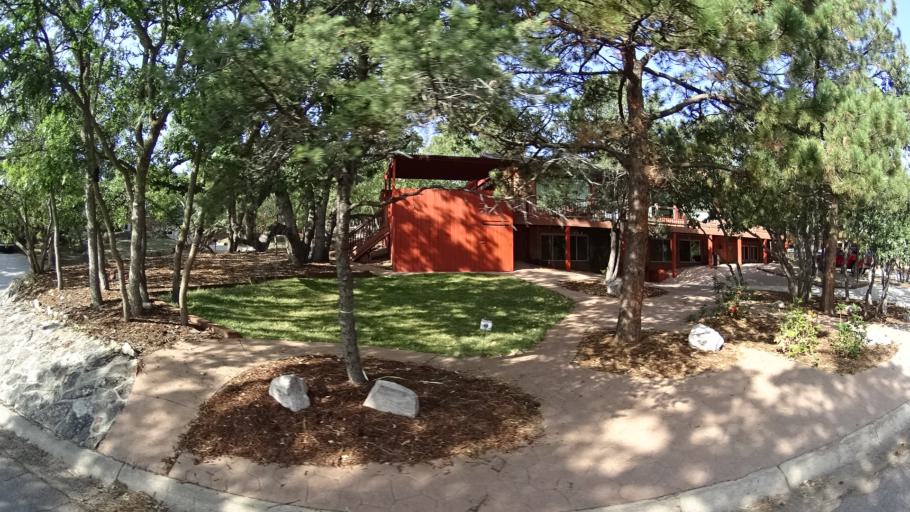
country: US
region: Colorado
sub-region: El Paso County
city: Colorado Springs
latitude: 38.8145
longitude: -104.8657
